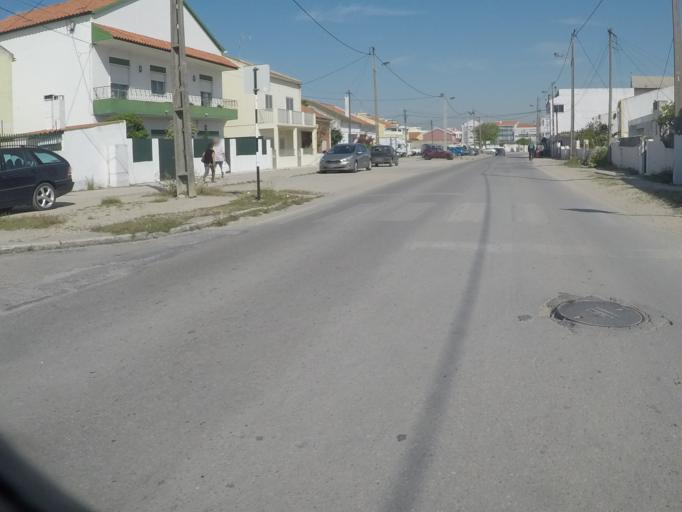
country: PT
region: Setubal
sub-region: Almada
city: Costa de Caparica
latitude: 38.6358
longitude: -9.2280
